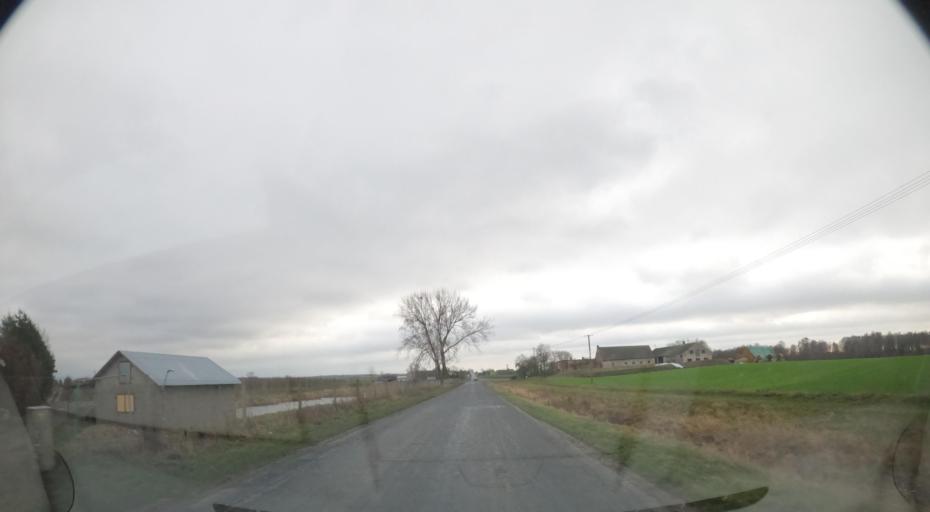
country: PL
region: Greater Poland Voivodeship
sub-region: Powiat pilski
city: Lobzenica
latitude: 53.2220
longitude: 17.3378
